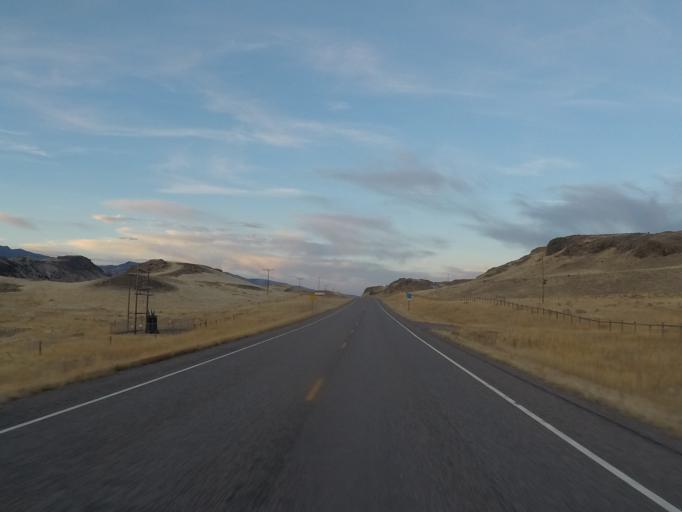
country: US
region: Montana
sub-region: Gallatin County
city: Bozeman
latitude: 45.2332
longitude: -110.8747
